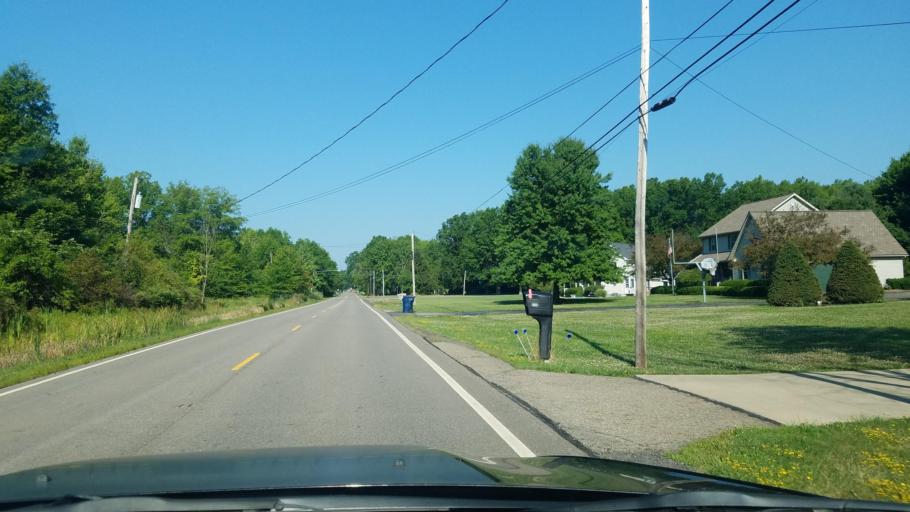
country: US
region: Ohio
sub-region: Trumbull County
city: Champion Heights
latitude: 41.3084
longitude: -80.8765
